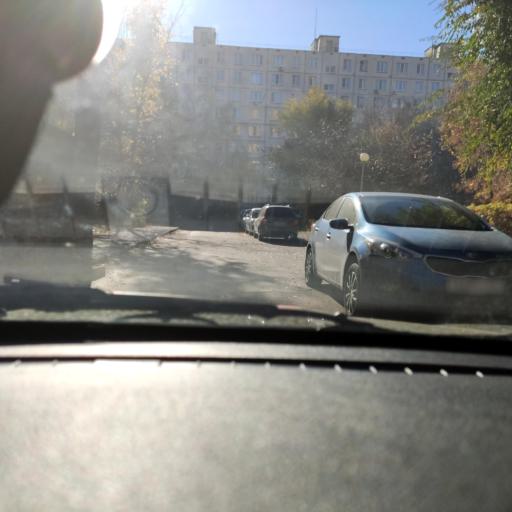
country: RU
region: Samara
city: Tol'yatti
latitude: 53.5092
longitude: 49.2869
